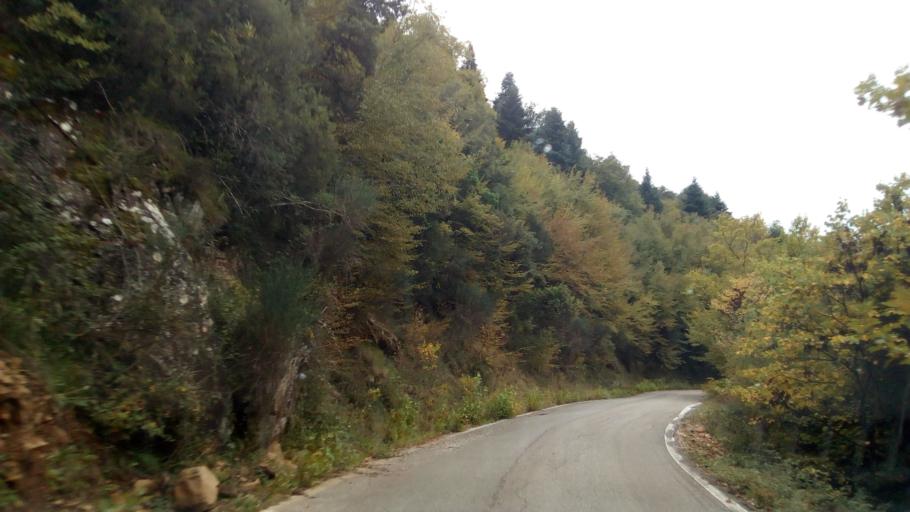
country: GR
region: West Greece
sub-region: Nomos Aitolias kai Akarnanias
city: Thermo
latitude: 38.5898
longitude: 21.8490
